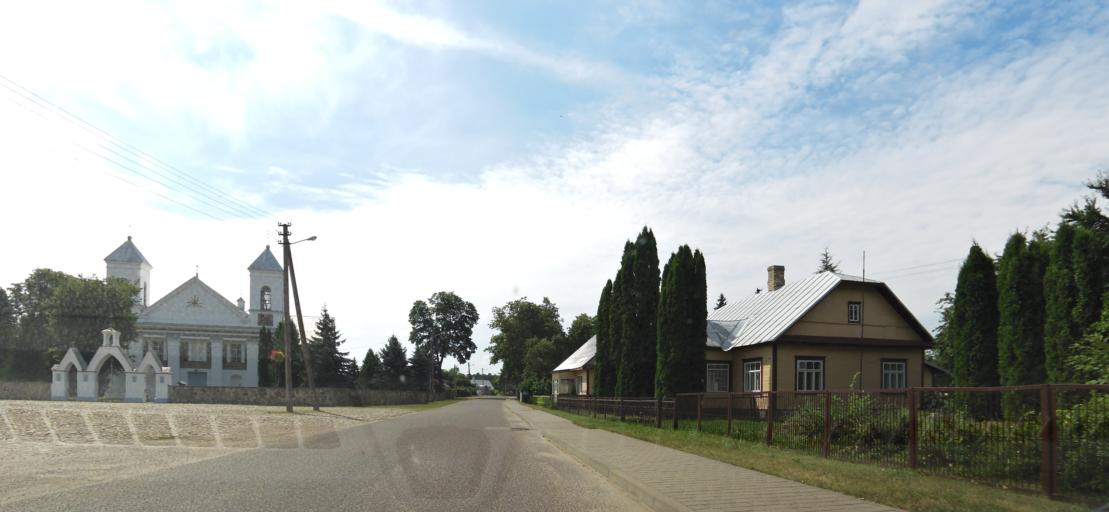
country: LT
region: Vilnius County
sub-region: Trakai
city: Rudiskes
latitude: 54.3589
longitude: 24.8404
